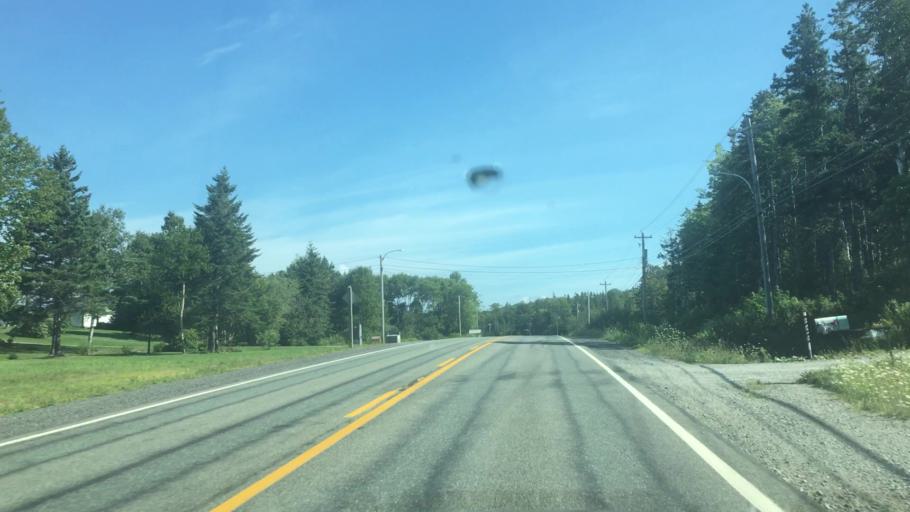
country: CA
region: Nova Scotia
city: Sydney
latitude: 45.9952
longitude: -60.4070
